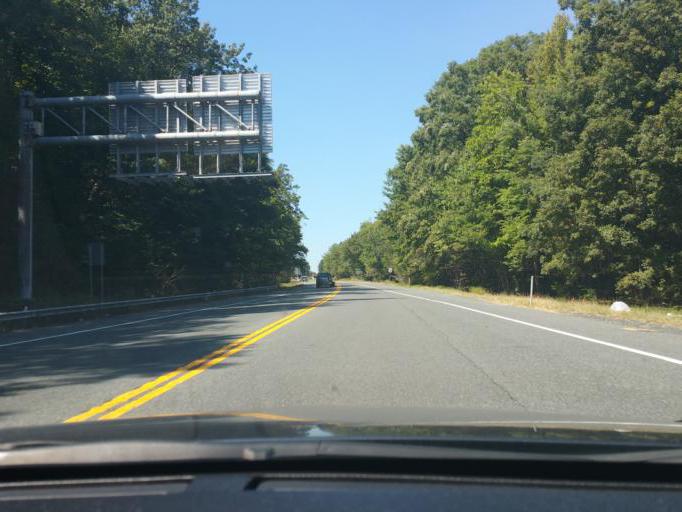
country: US
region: Maryland
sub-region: Harford County
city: Havre de Grace
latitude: 39.5738
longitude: -76.1435
